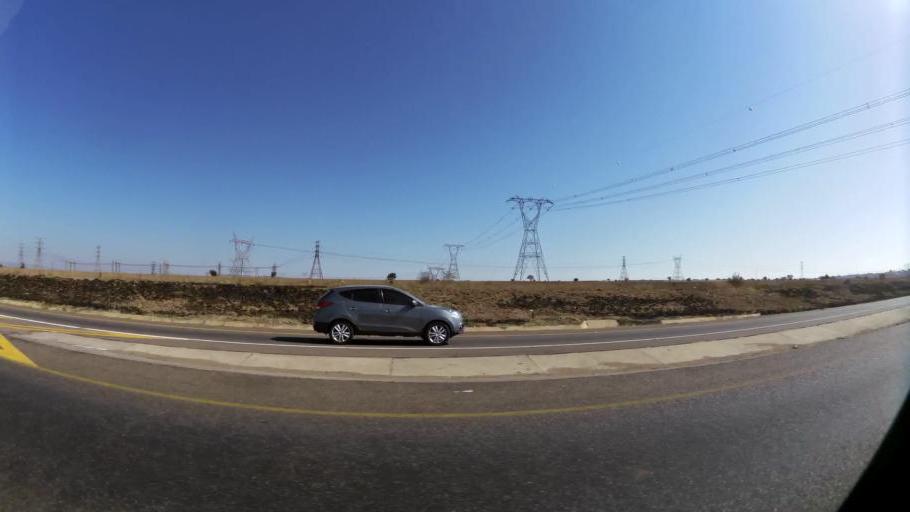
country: ZA
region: Gauteng
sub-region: City of Tshwane Metropolitan Municipality
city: Mabopane
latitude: -25.5609
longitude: 28.1076
